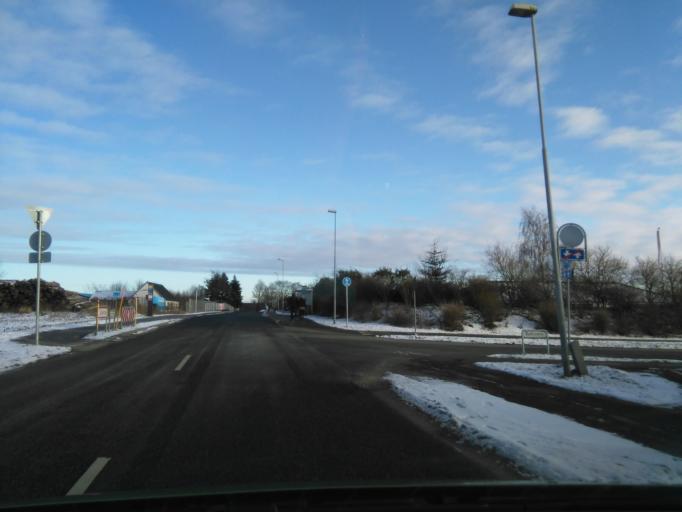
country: DK
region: Central Jutland
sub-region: Arhus Kommune
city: Framlev
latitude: 56.1480
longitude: 9.9864
